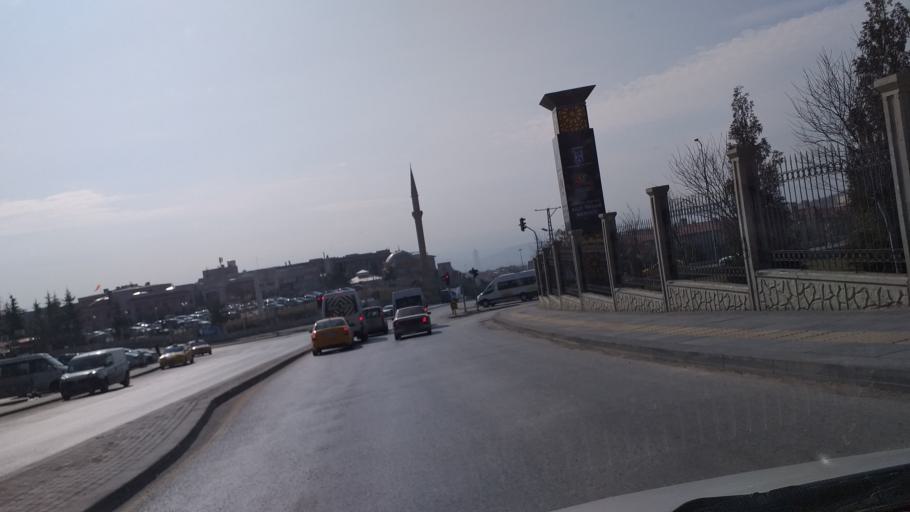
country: TR
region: Ankara
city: Mamak
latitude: 40.0043
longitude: 32.8554
